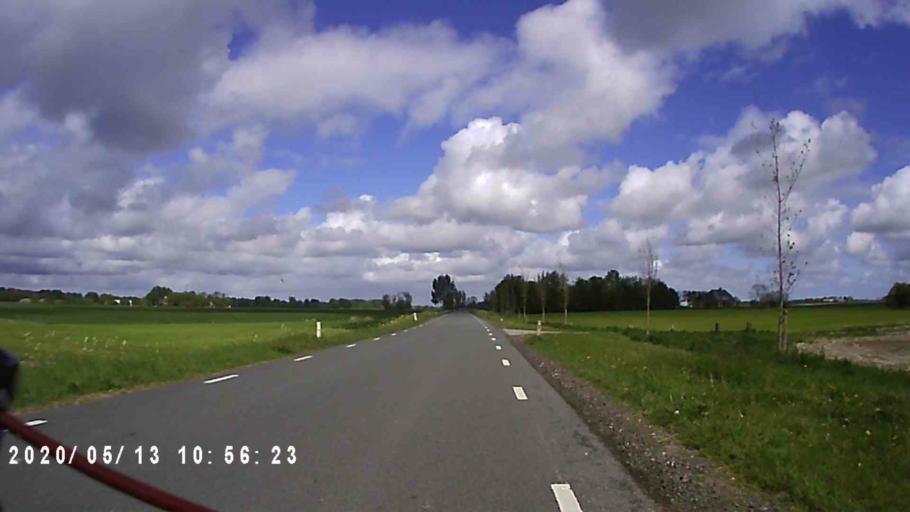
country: NL
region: Groningen
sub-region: Gemeente Zuidhorn
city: Grijpskerk
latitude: 53.2701
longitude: 6.3361
